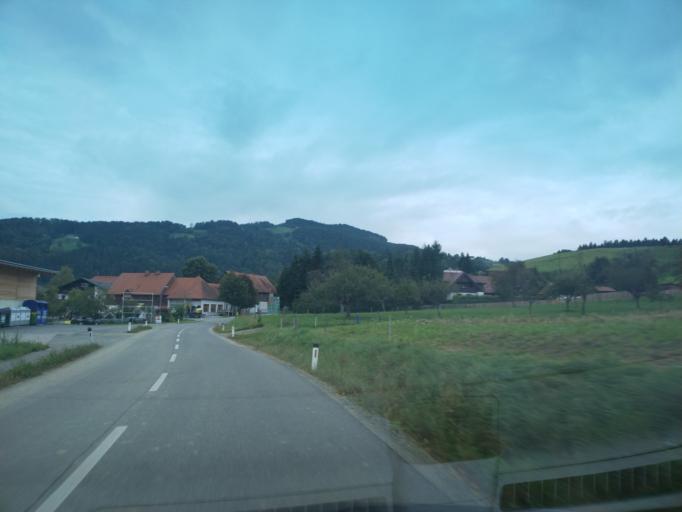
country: AT
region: Styria
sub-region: Politischer Bezirk Deutschlandsberg
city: Wernersdorf
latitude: 46.7164
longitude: 15.2094
